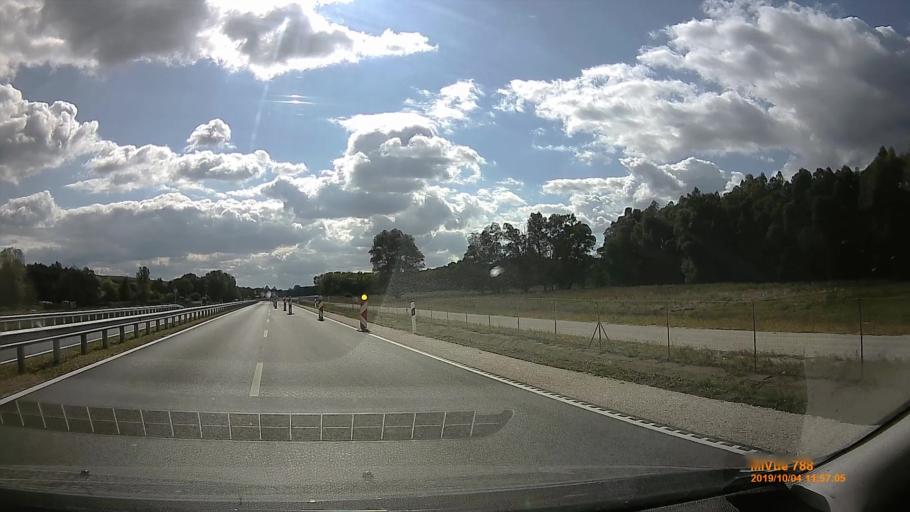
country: HU
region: Somogy
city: Karad
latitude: 46.6640
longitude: 17.7837
